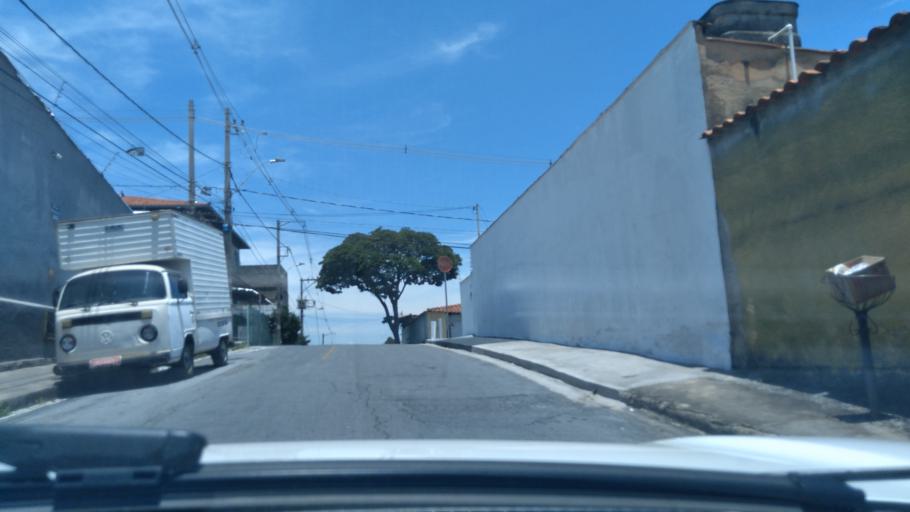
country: BR
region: Minas Gerais
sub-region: Contagem
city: Contagem
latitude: -19.9347
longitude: -44.0005
